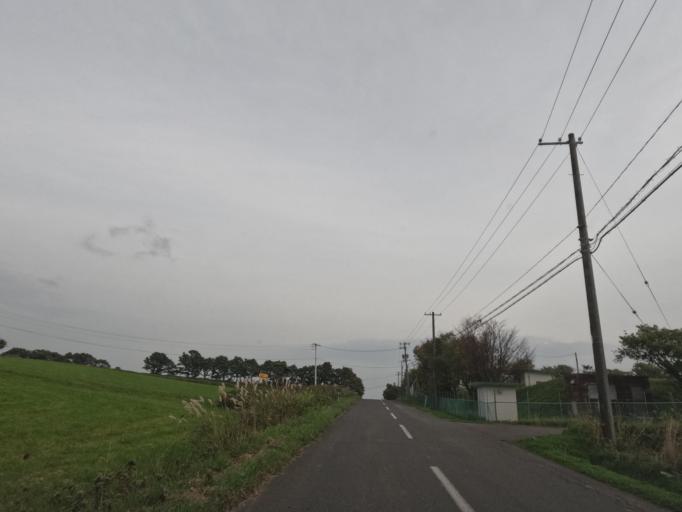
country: JP
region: Hokkaido
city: Date
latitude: 42.4077
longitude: 140.9207
